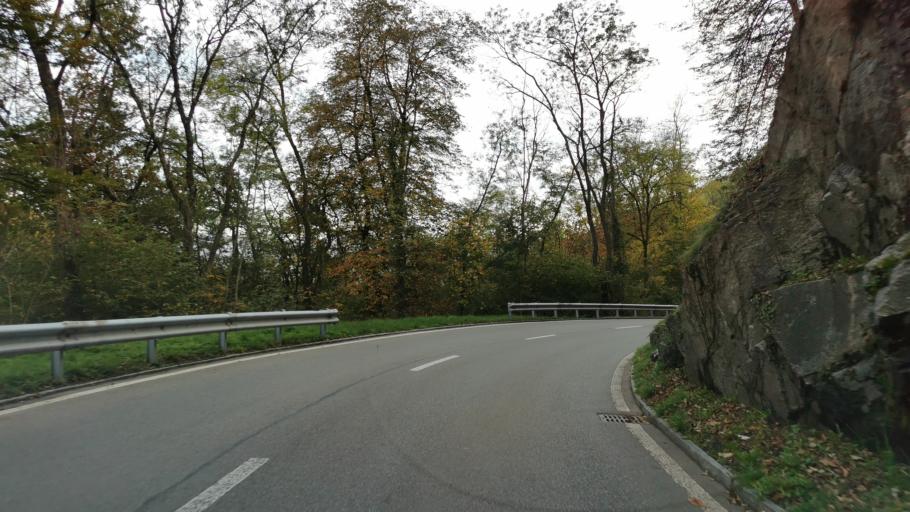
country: CH
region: Ticino
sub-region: Lugano District
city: Pura
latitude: 46.0001
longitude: 8.8604
